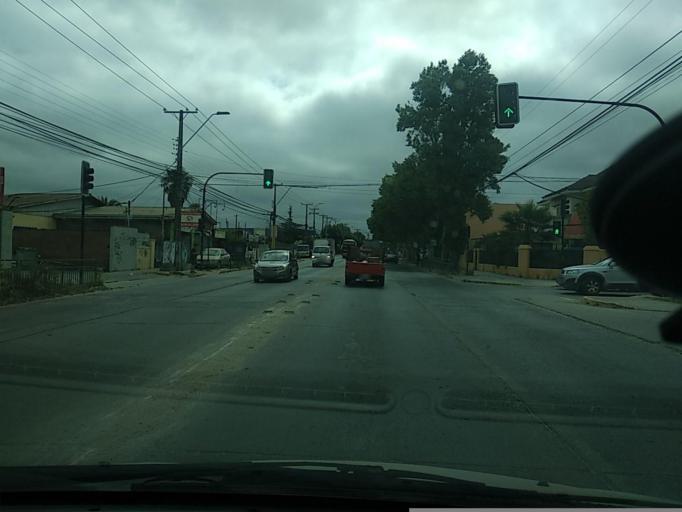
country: CL
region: Valparaiso
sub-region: Provincia de Marga Marga
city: Villa Alemana
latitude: -33.0447
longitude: -71.3858
